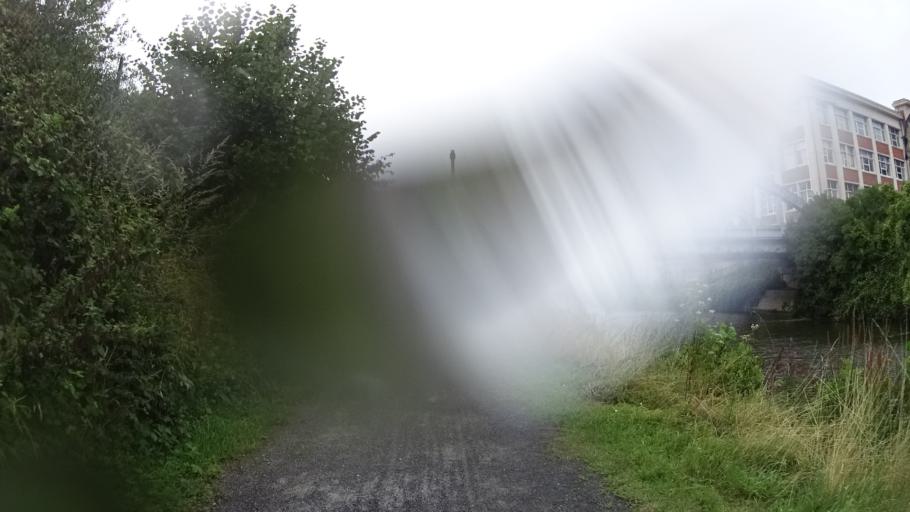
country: FR
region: Nord-Pas-de-Calais
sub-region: Departement du Nord
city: Louvroil
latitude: 50.2663
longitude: 3.9556
